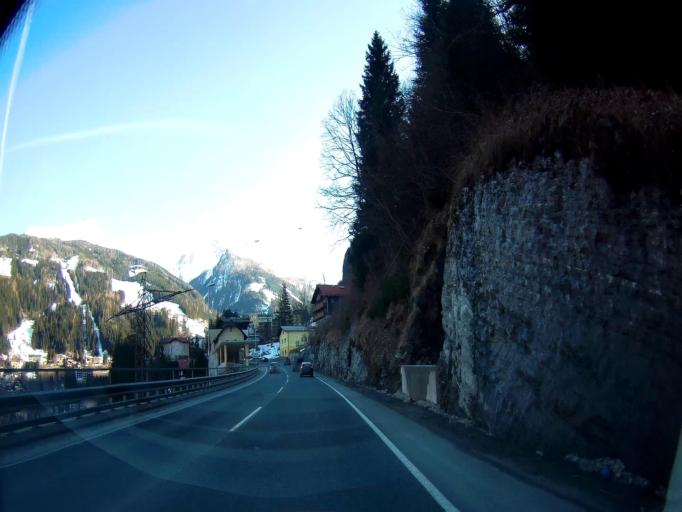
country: AT
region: Salzburg
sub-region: Politischer Bezirk Sankt Johann im Pongau
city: Bad Gastein
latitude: 47.1225
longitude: 13.1314
